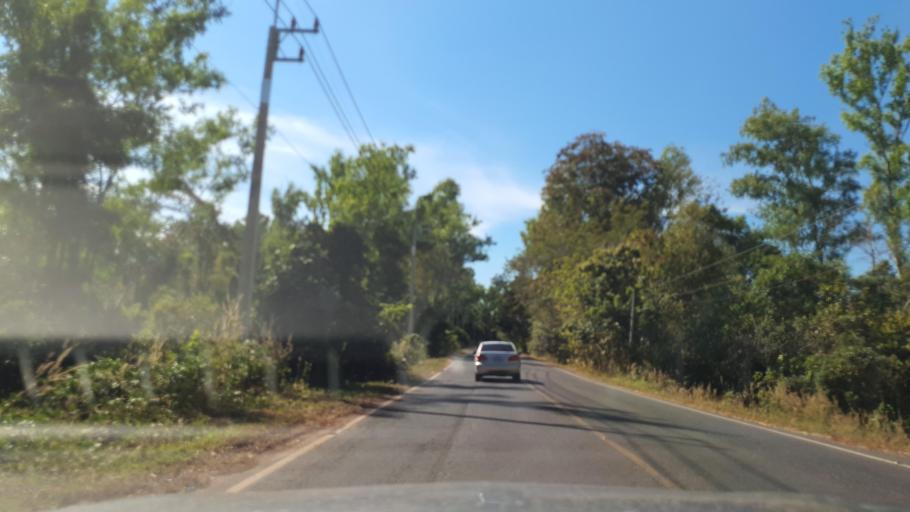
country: TH
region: Kalasin
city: Khao Wong
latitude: 16.7642
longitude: 104.1436
